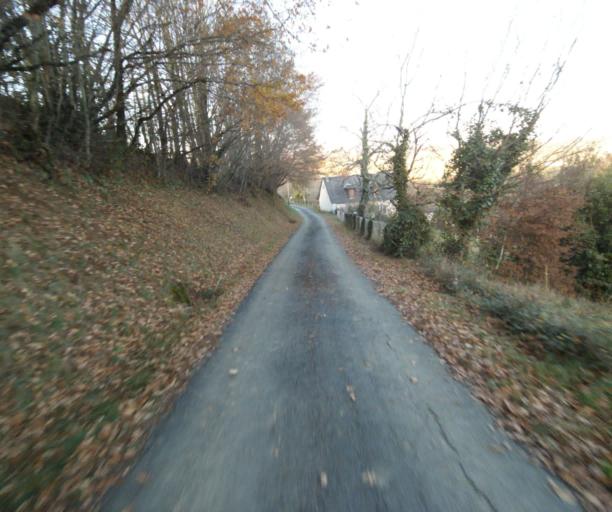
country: FR
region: Limousin
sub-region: Departement de la Correze
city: Laguenne
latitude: 45.2291
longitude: 1.8277
